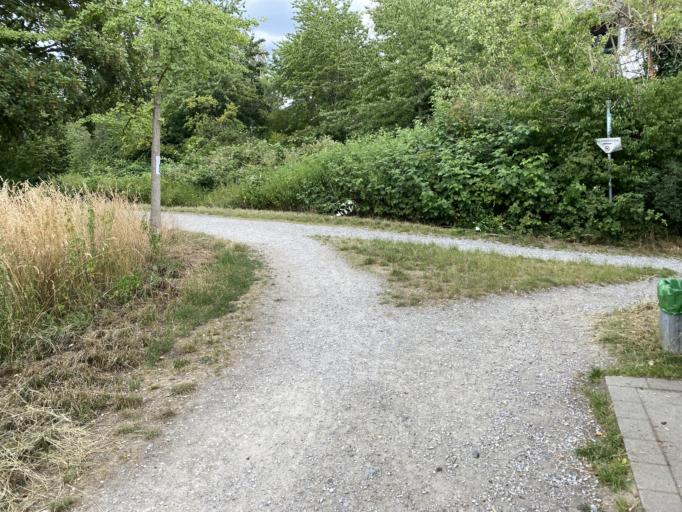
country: DE
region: North Rhine-Westphalia
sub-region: Regierungsbezirk Dusseldorf
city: Essen
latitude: 51.4154
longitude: 7.0296
